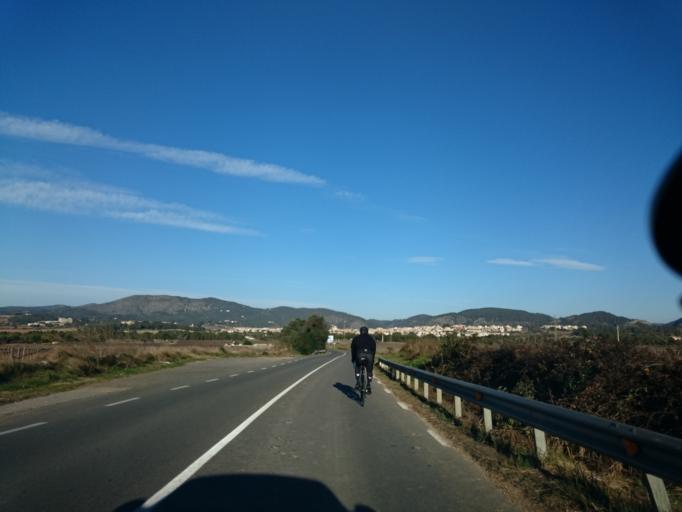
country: ES
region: Catalonia
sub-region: Provincia de Barcelona
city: Sitges
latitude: 41.2468
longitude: 1.7891
